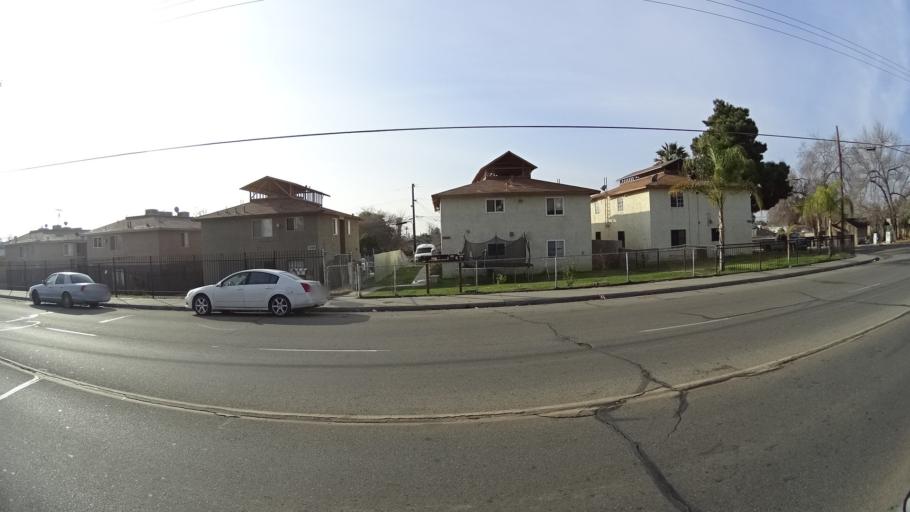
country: US
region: California
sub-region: Kern County
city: Bakersfield
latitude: 35.3892
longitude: -118.9779
